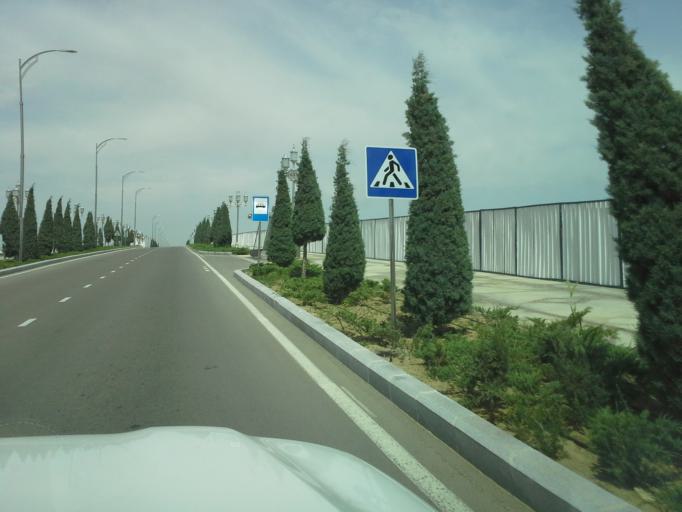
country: TM
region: Balkan
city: Turkmenbasy
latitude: 39.9650
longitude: 52.8374
